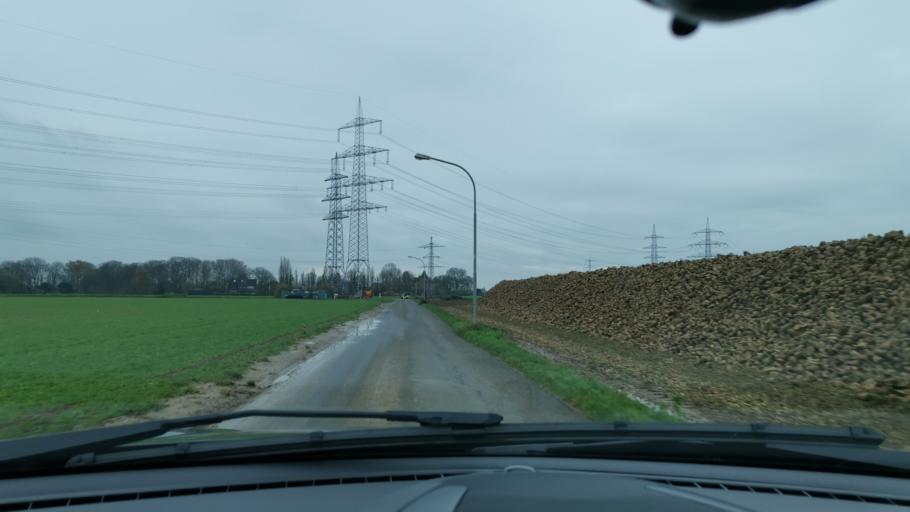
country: DE
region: North Rhine-Westphalia
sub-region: Regierungsbezirk Dusseldorf
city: Neubrueck
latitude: 51.1179
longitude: 6.6950
